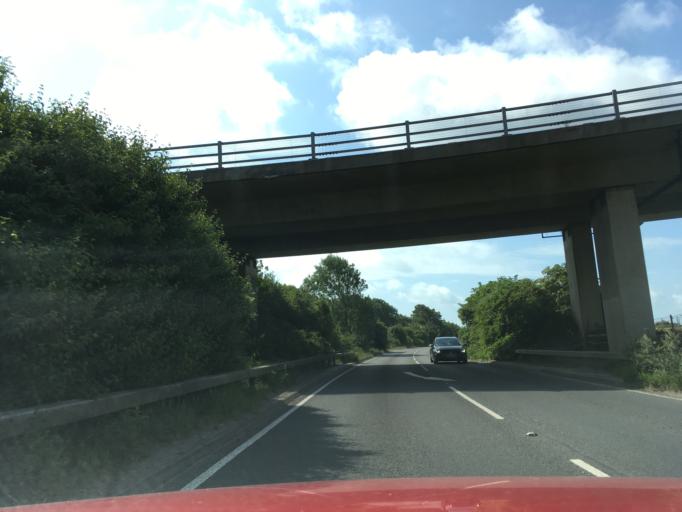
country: GB
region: England
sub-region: West Sussex
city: Shoreham-by-Sea
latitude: 50.8436
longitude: -0.2850
